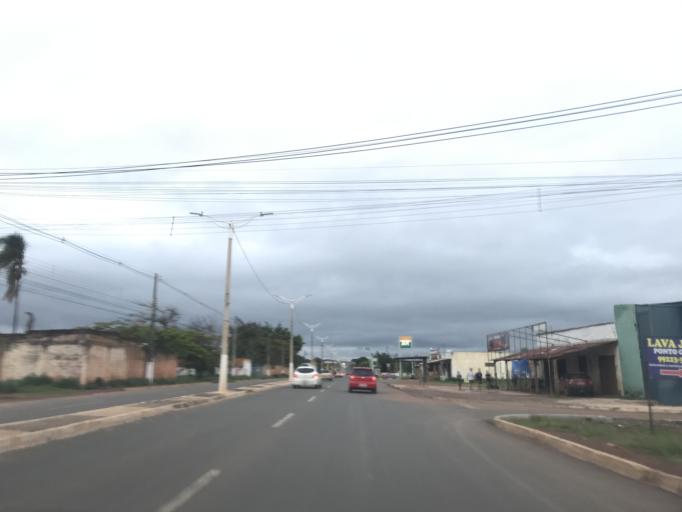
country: BR
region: Goias
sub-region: Luziania
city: Luziania
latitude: -16.2253
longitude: -47.9371
